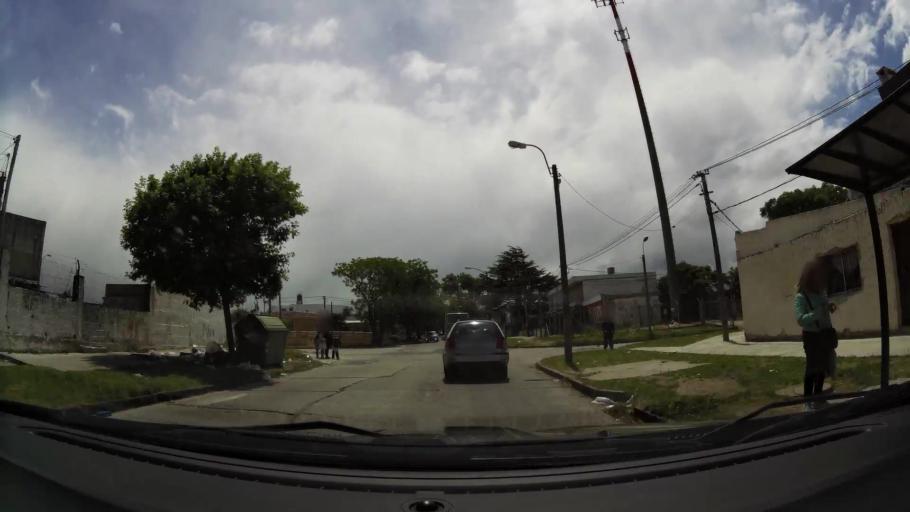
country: UY
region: Montevideo
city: Montevideo
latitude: -34.8791
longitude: -56.1274
